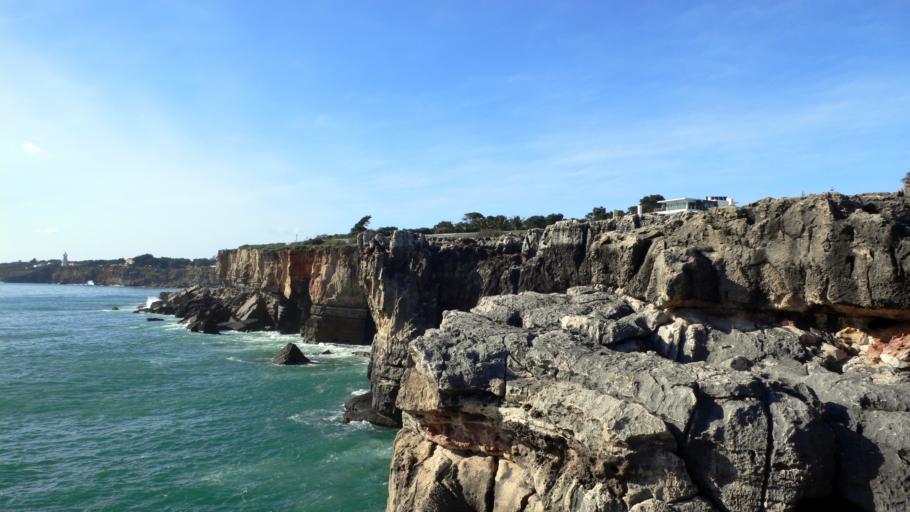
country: PT
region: Lisbon
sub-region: Cascais
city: Cascais
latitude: 38.6907
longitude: -9.4308
